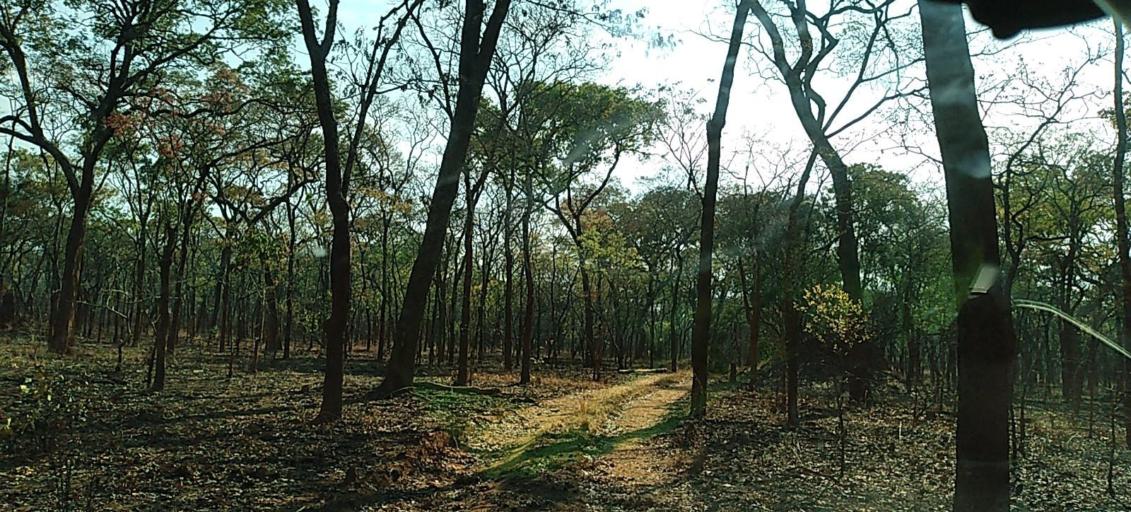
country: ZM
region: North-Western
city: Kalengwa
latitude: -13.2259
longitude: 25.0954
